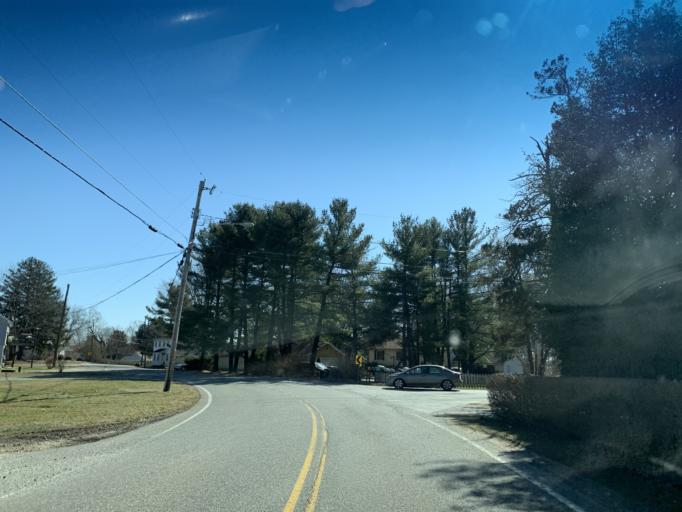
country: US
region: Maryland
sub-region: Cecil County
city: Perryville
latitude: 39.6026
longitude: -76.0718
